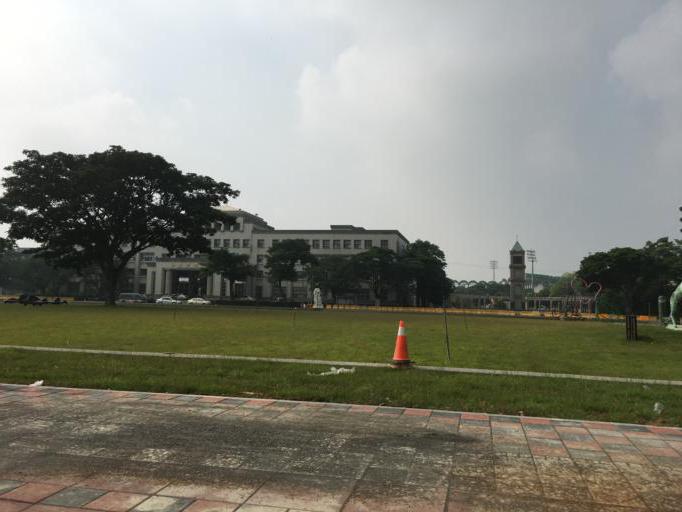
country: TW
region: Taiwan
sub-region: Chiayi
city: Taibao
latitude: 23.4603
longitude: 120.2926
